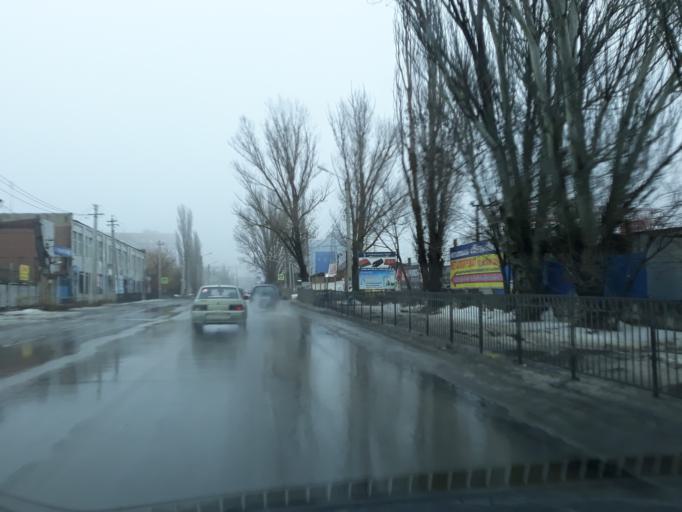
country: RU
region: Rostov
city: Taganrog
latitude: 47.2137
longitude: 38.8746
